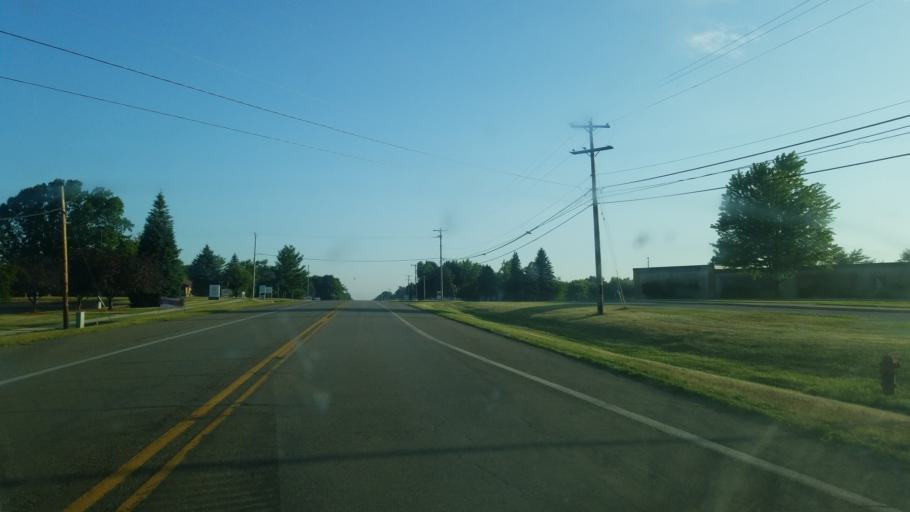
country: US
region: Michigan
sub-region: Montcalm County
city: Stanton
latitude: 43.2987
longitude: -85.0848
